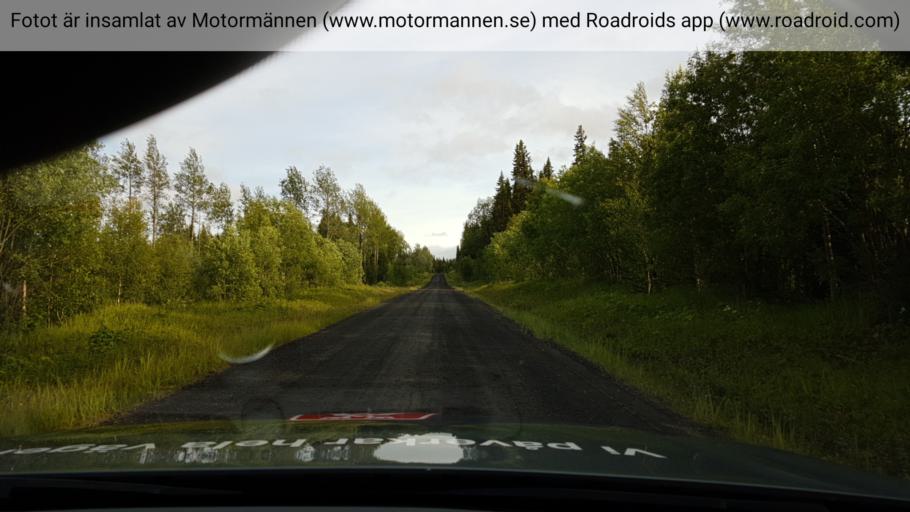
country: SE
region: Jaemtland
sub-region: OEstersunds Kommun
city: Lit
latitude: 63.6501
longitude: 15.0716
